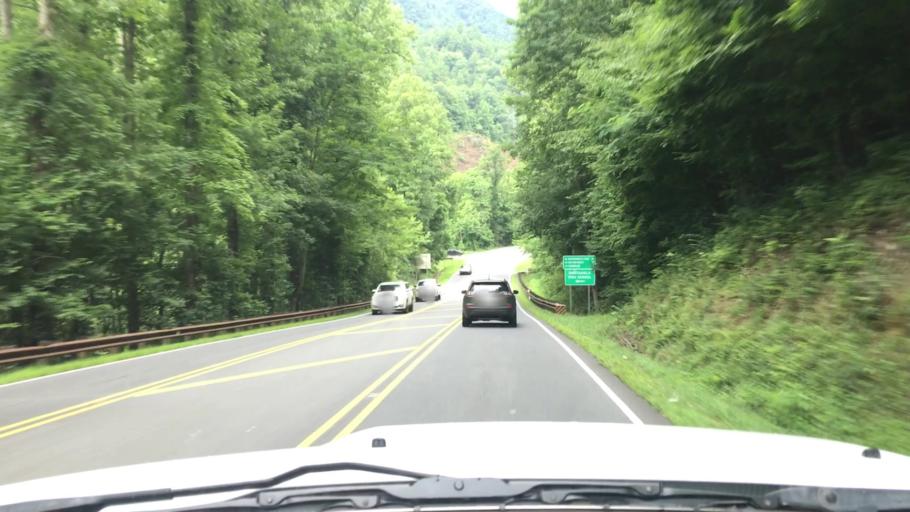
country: US
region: North Carolina
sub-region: Graham County
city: Robbinsville
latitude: 35.2755
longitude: -83.6823
